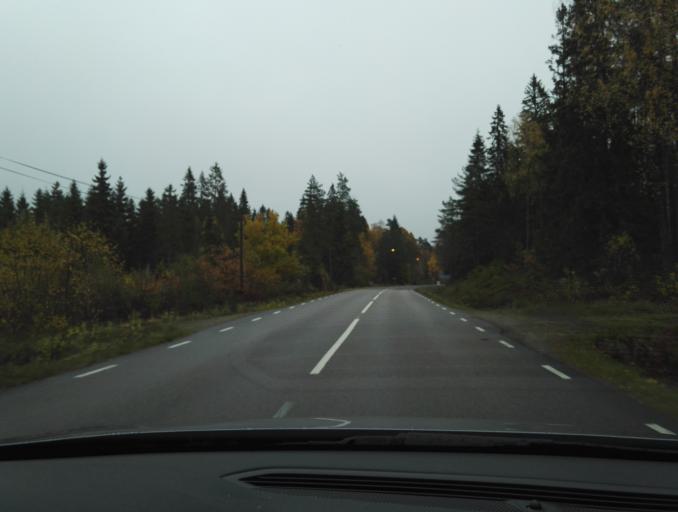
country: SE
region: Kronoberg
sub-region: Vaxjo Kommun
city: Rottne
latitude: 57.0239
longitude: 14.8319
